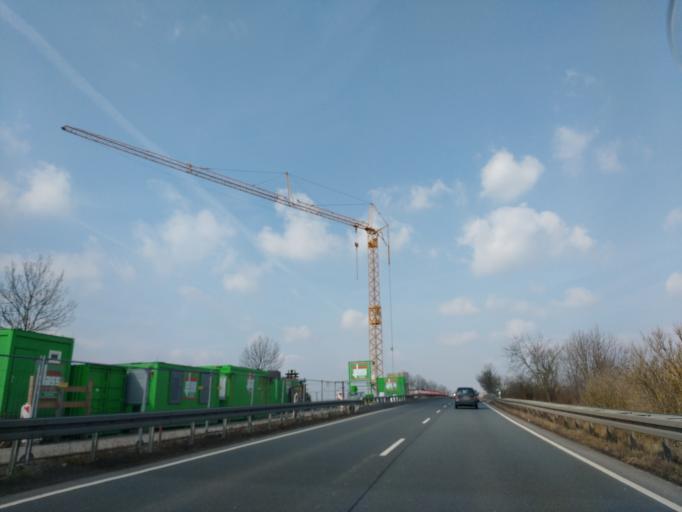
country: DE
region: Saxony-Anhalt
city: Wansleben
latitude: 51.4742
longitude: 11.7238
